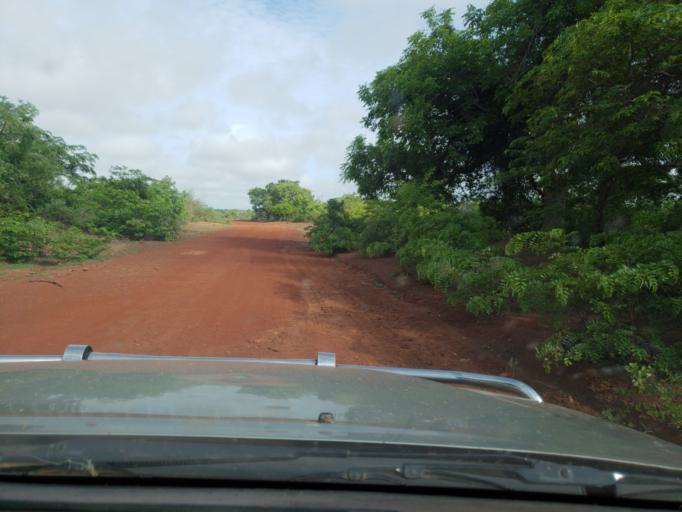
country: ML
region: Sikasso
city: Koutiala
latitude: 12.3929
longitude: -5.9785
